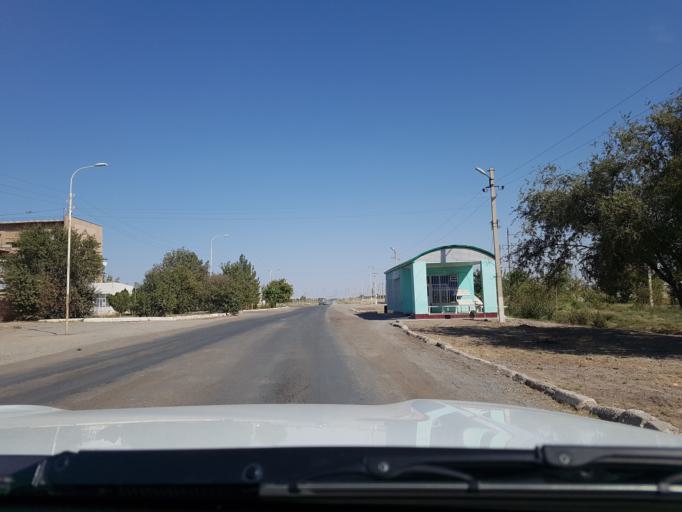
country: IR
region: Razavi Khorasan
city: Sarakhs
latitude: 36.5238
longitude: 61.2263
